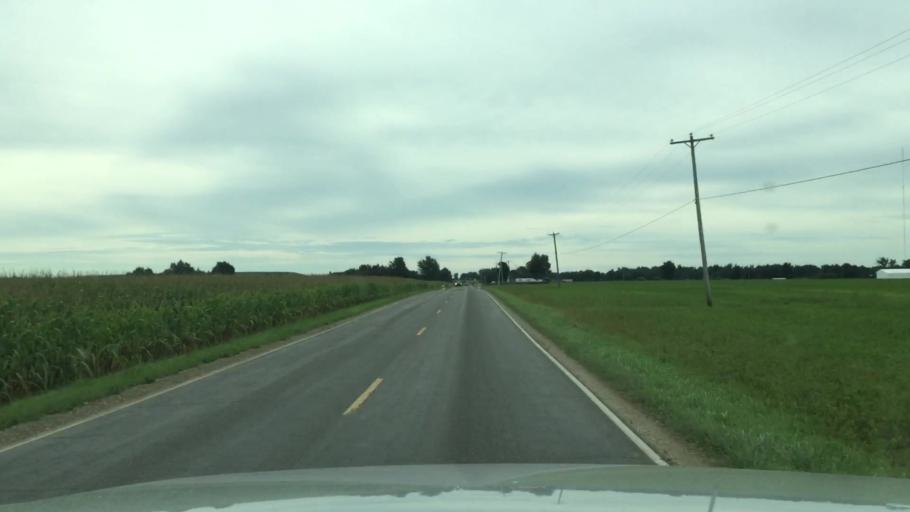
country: US
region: Michigan
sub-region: Shiawassee County
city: Durand
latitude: 43.0060
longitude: -83.9870
